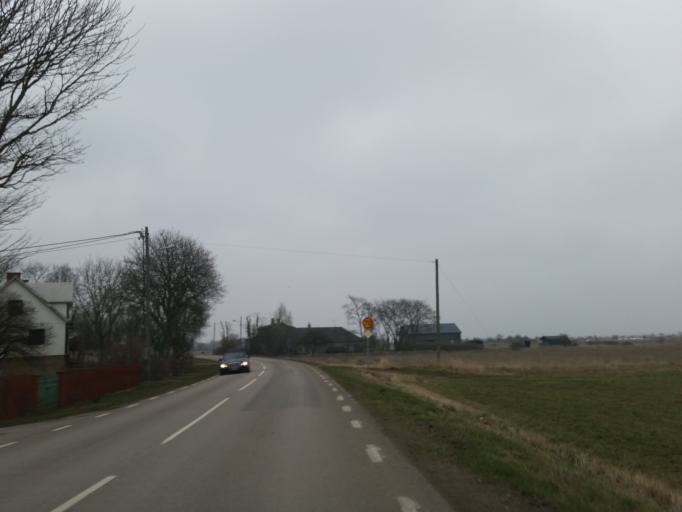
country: SE
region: Kalmar
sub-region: Morbylanga Kommun
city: Moerbylanga
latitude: 56.3209
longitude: 16.5186
